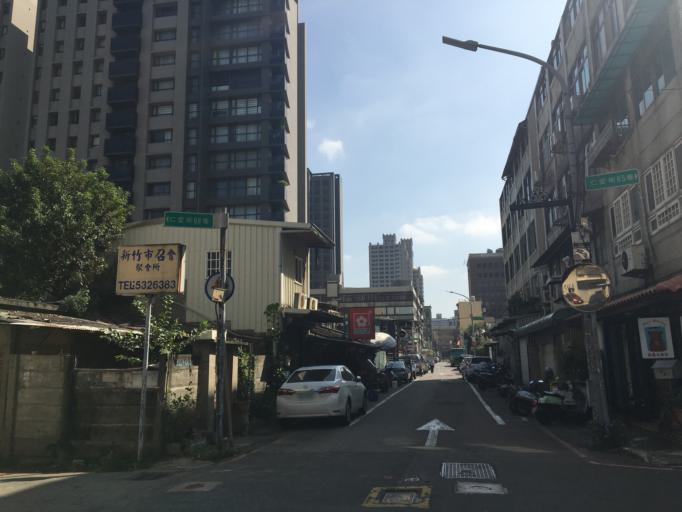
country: TW
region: Taiwan
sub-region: Hsinchu
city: Hsinchu
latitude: 24.8081
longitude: 120.9706
